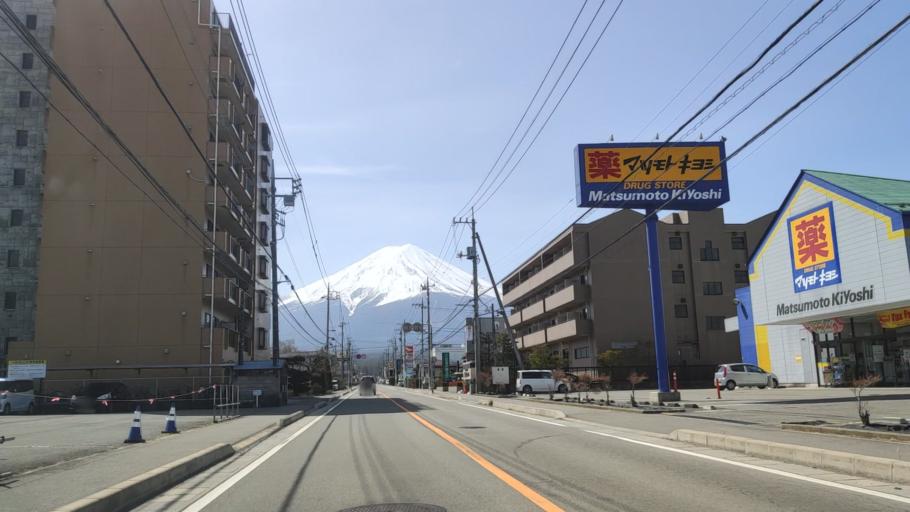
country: JP
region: Yamanashi
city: Fujikawaguchiko
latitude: 35.4951
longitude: 138.7642
